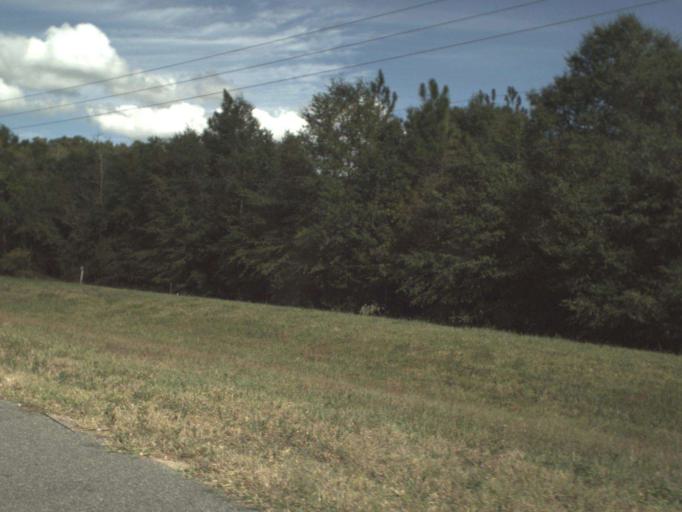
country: US
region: Florida
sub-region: Okaloosa County
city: Crestview
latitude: 30.7323
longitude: -86.6540
